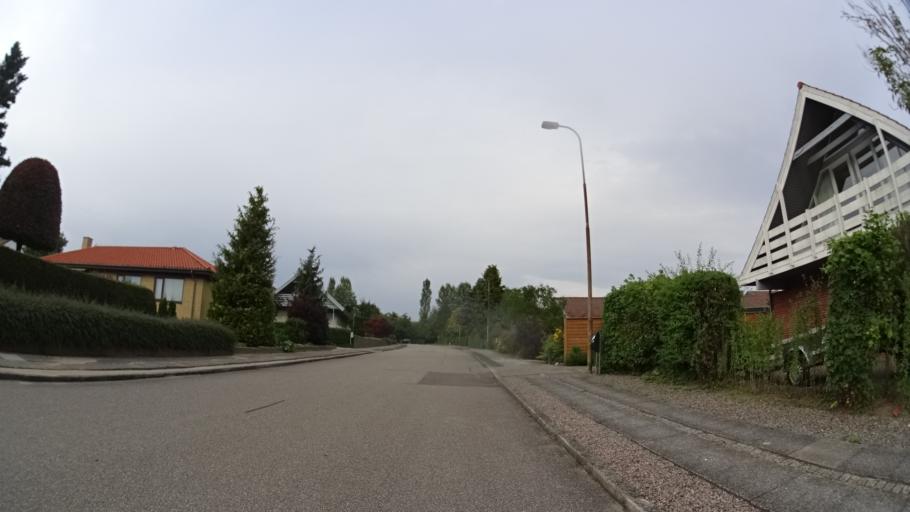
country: DK
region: Central Jutland
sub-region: Arhus Kommune
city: Stavtrup
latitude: 56.1469
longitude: 10.1353
